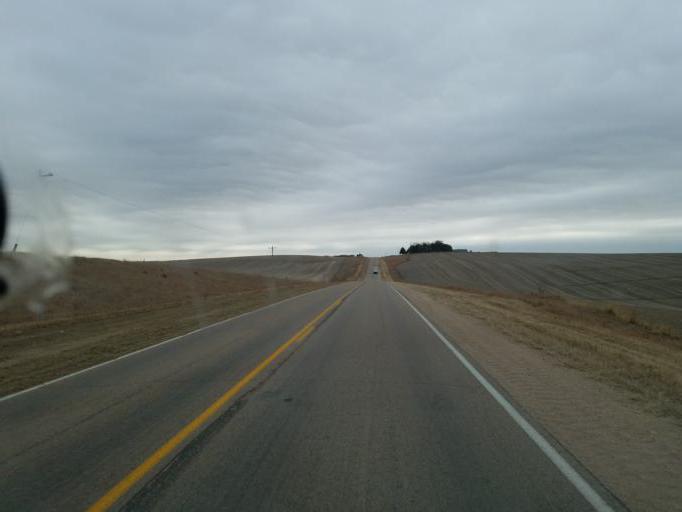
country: US
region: Nebraska
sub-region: Cedar County
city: Hartington
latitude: 42.4877
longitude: -97.2113
